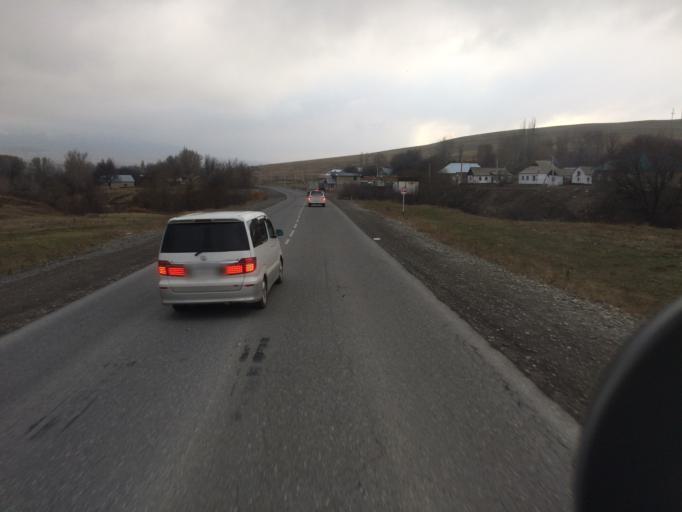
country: KZ
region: Ongtustik Qazaqstan
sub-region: Tulkibas Audany
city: Zhabagly
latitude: 42.5186
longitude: 70.5853
